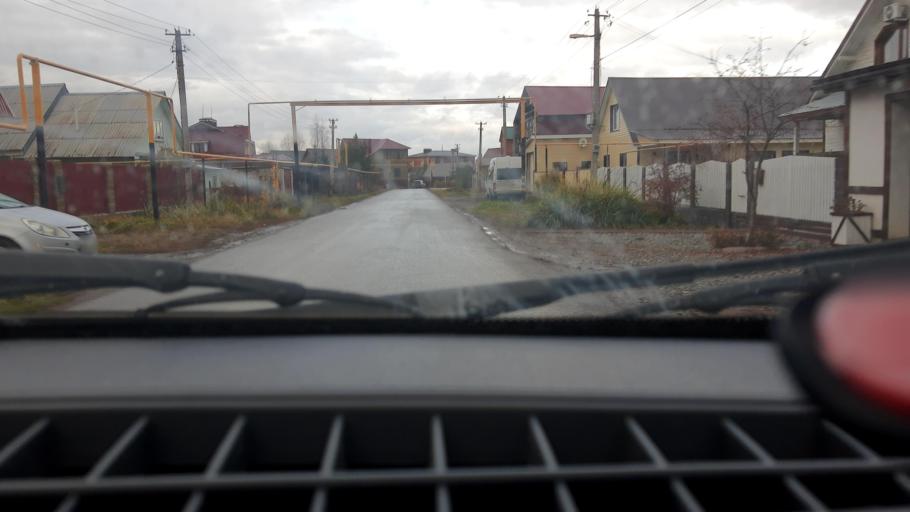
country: RU
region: Bashkortostan
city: Mikhaylovka
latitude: 54.8064
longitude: 55.9391
